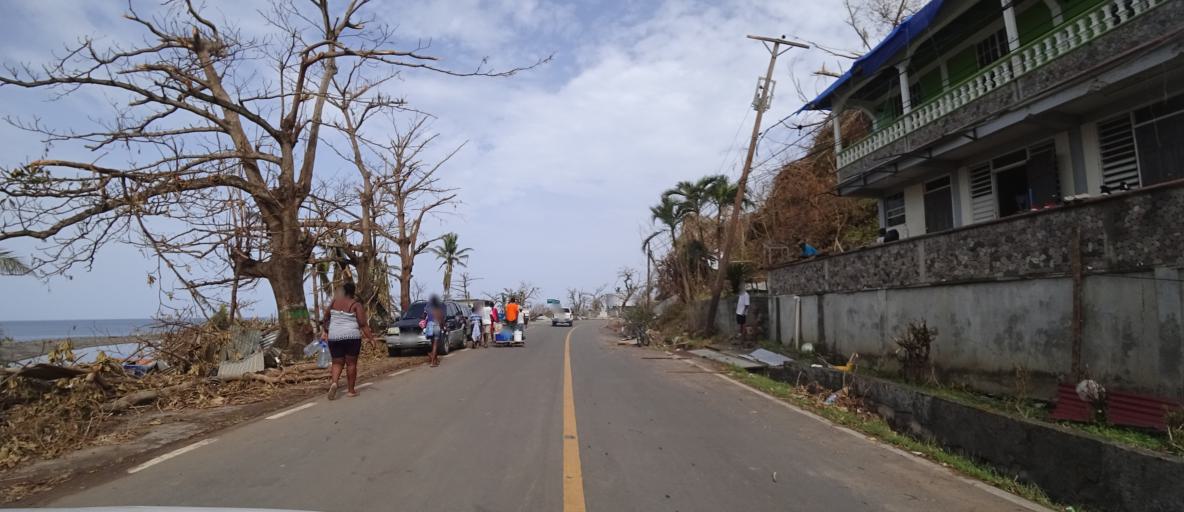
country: DM
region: Saint Paul
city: Mahaut
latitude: 15.3645
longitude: -61.4016
